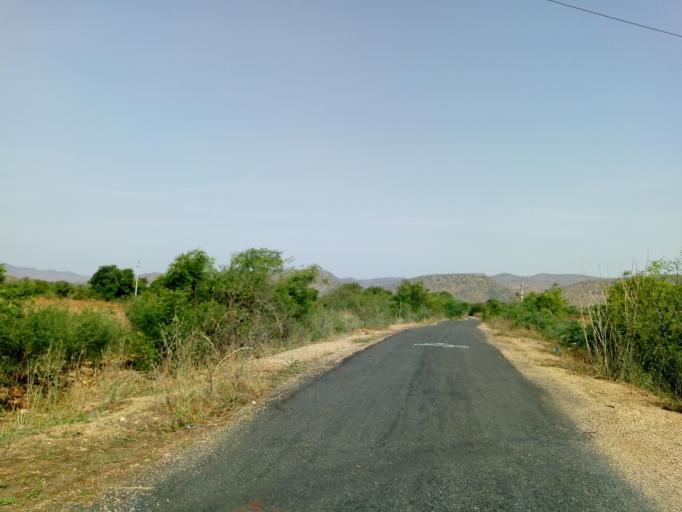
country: IN
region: Andhra Pradesh
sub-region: Prakasam
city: Cumbum
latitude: 15.7135
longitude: 79.0832
